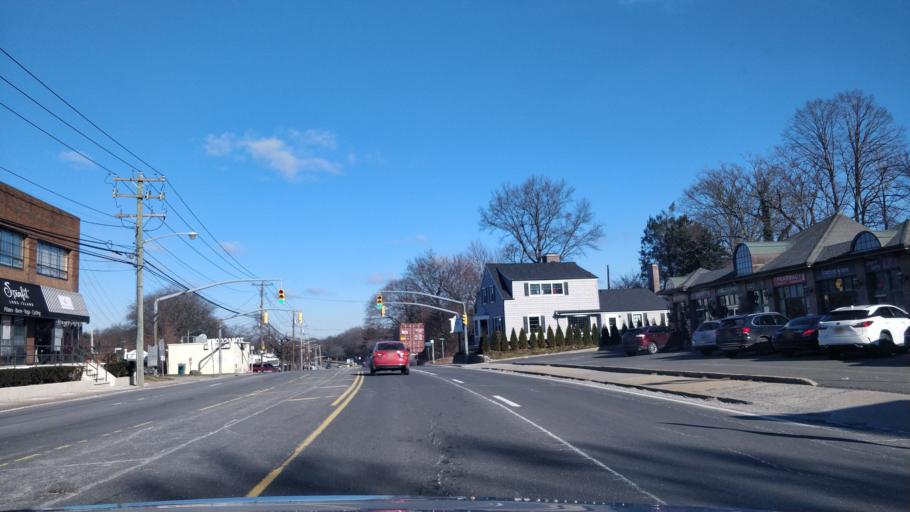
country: US
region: New York
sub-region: Nassau County
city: Greenvale
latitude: 40.8142
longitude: -73.6267
